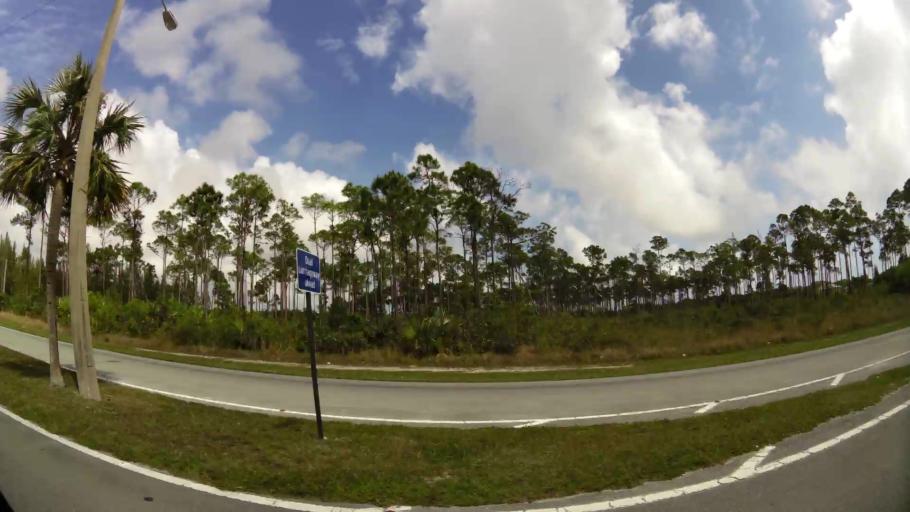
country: BS
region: Freeport
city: Freeport
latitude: 26.5106
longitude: -78.6954
